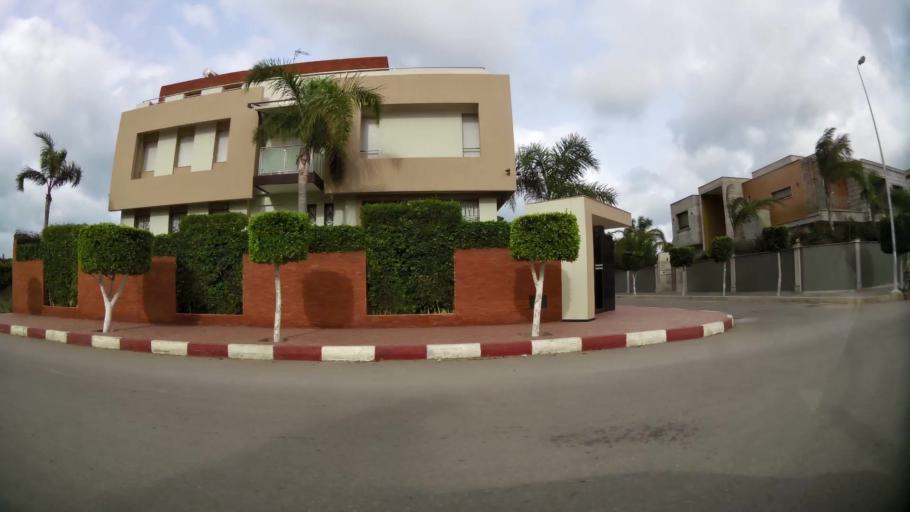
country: MA
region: Oriental
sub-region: Nador
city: Nador
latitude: 35.1626
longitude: -2.9164
